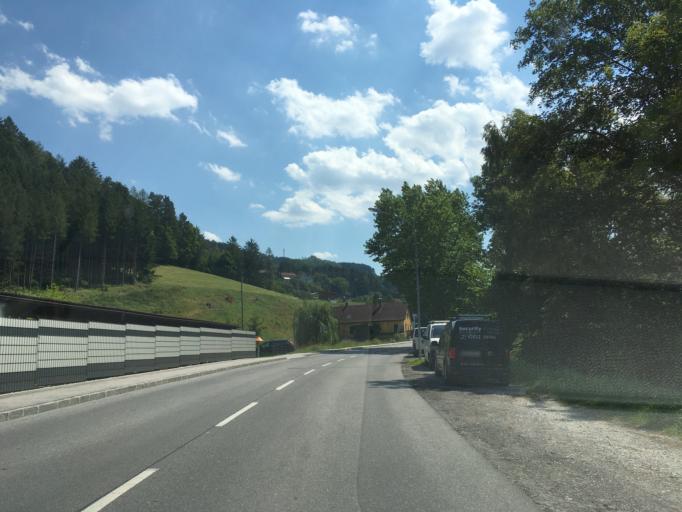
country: AT
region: Lower Austria
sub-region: Politischer Bezirk Neunkirchen
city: Edlitz
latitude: 47.5949
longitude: 16.1446
